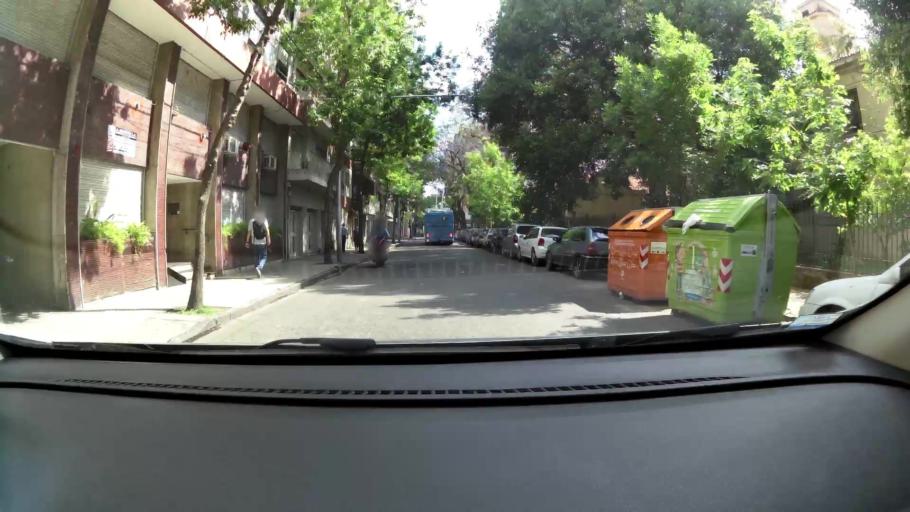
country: AR
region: Santa Fe
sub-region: Departamento de Rosario
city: Rosario
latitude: -32.9560
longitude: -60.6260
